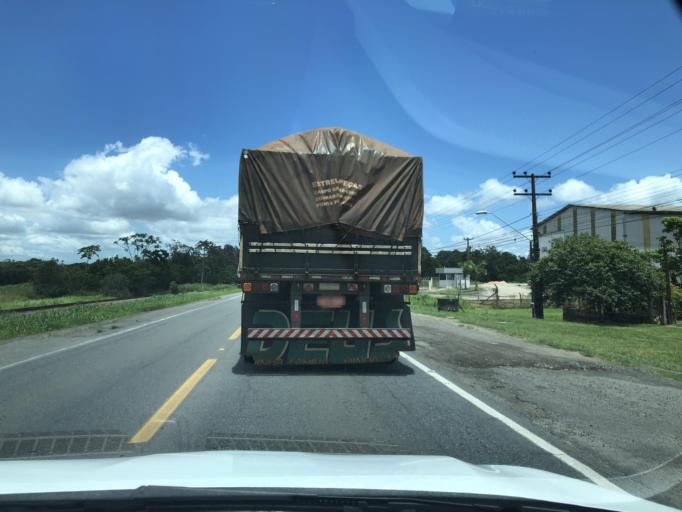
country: BR
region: Santa Catarina
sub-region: Sao Francisco Do Sul
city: Sao Francisco do Sul
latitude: -26.3706
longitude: -48.6959
